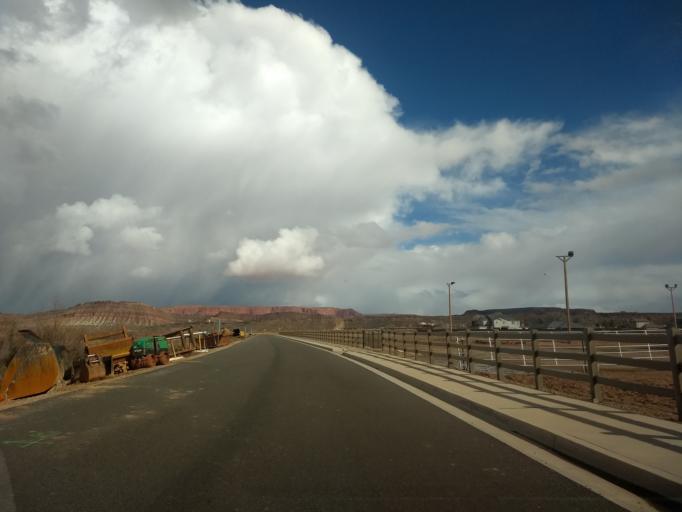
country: US
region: Utah
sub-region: Washington County
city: Washington
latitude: 37.0669
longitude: -113.5210
